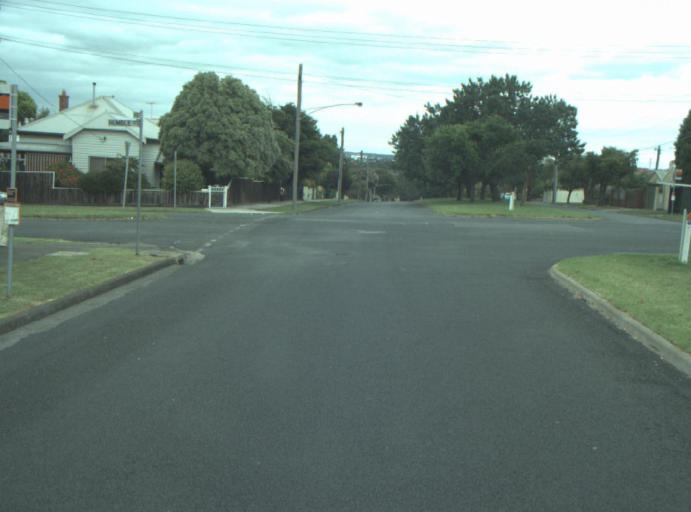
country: AU
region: Victoria
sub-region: Greater Geelong
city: East Geelong
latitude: -38.1576
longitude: 144.3809
